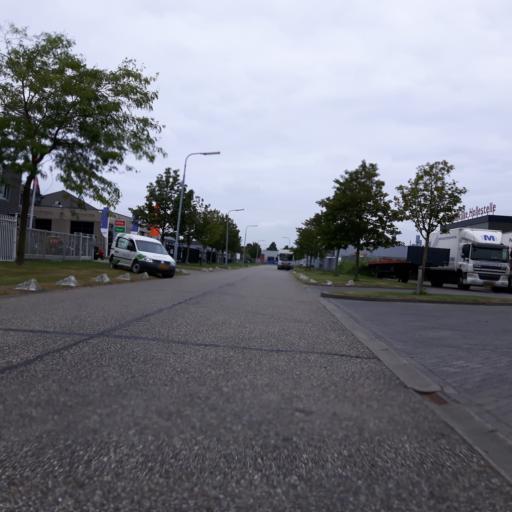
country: NL
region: Zeeland
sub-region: Gemeente Goes
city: Goes
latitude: 51.4881
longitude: 3.8736
